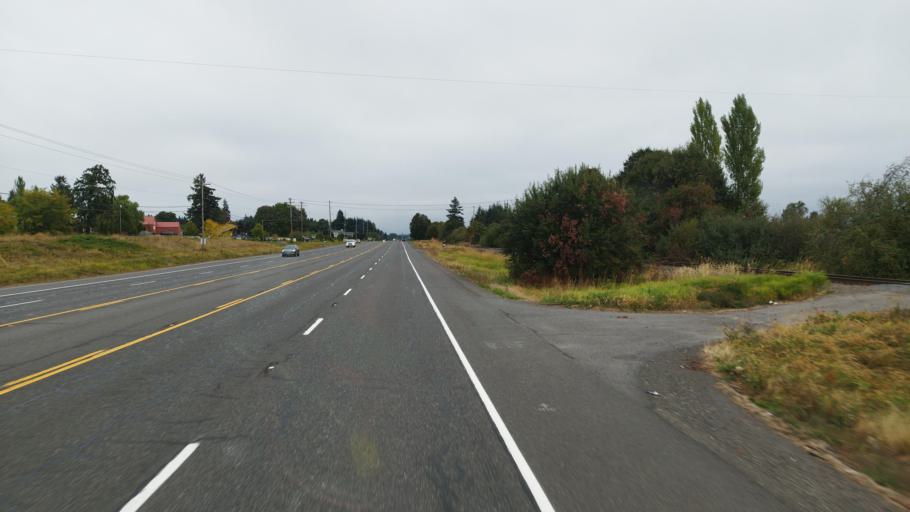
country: US
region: Oregon
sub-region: Columbia County
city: Warren
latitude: 45.8062
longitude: -122.8582
